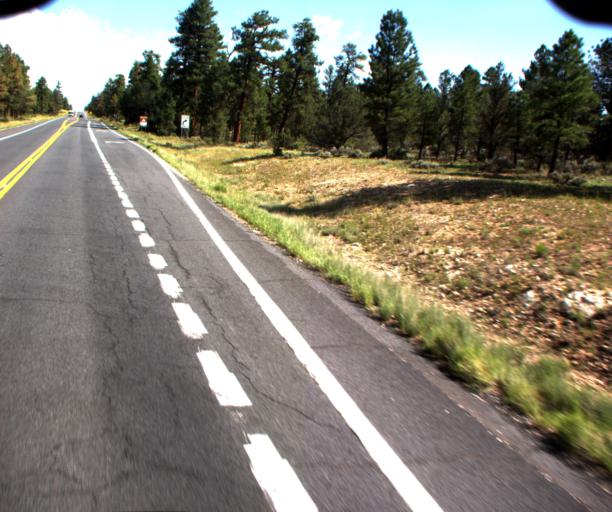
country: US
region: Arizona
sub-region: Coconino County
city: Grand Canyon Village
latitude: 35.9353
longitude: -112.1308
